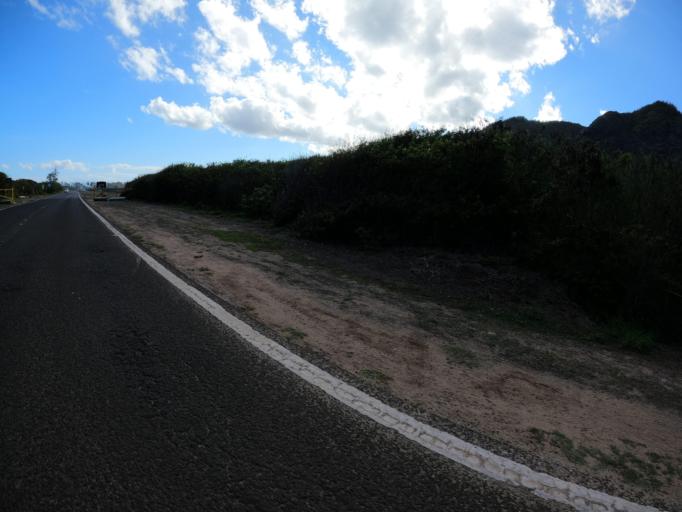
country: US
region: Hawaii
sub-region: Honolulu County
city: Mokuleia
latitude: 21.5796
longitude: -158.2142
